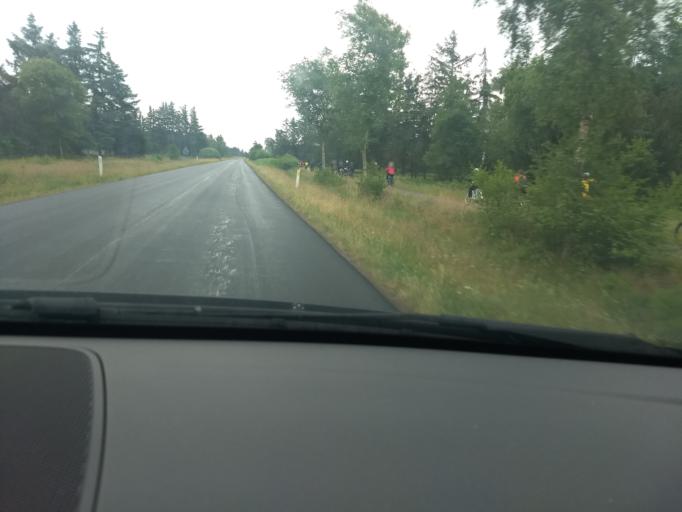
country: DK
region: South Denmark
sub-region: Fano Kommune
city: Nordby
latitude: 55.3762
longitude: 8.4492
